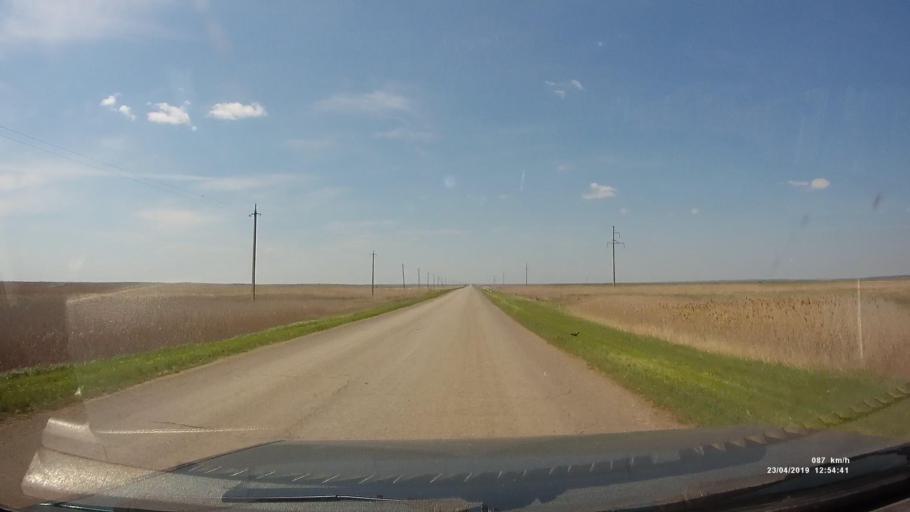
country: RU
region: Kalmykiya
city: Yashalta
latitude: 46.5815
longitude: 42.5745
